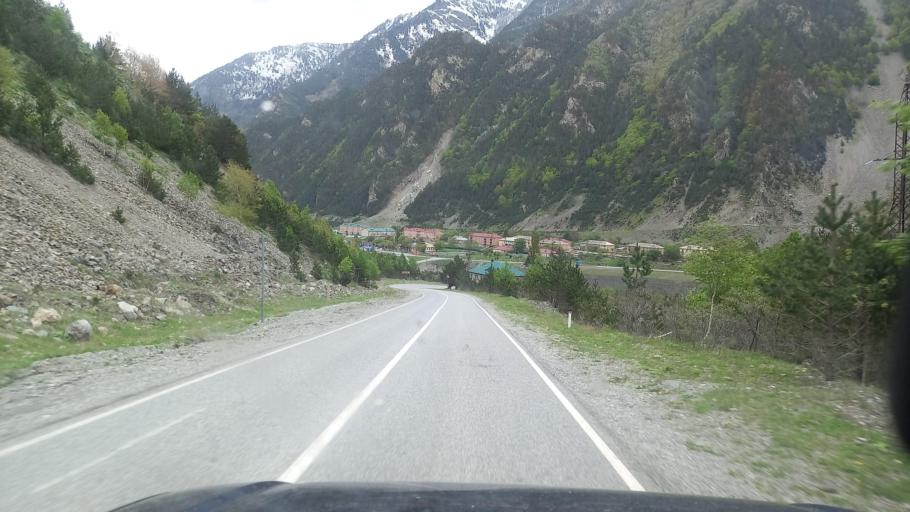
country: RU
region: North Ossetia
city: Mizur
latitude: 42.7919
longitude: 43.9993
